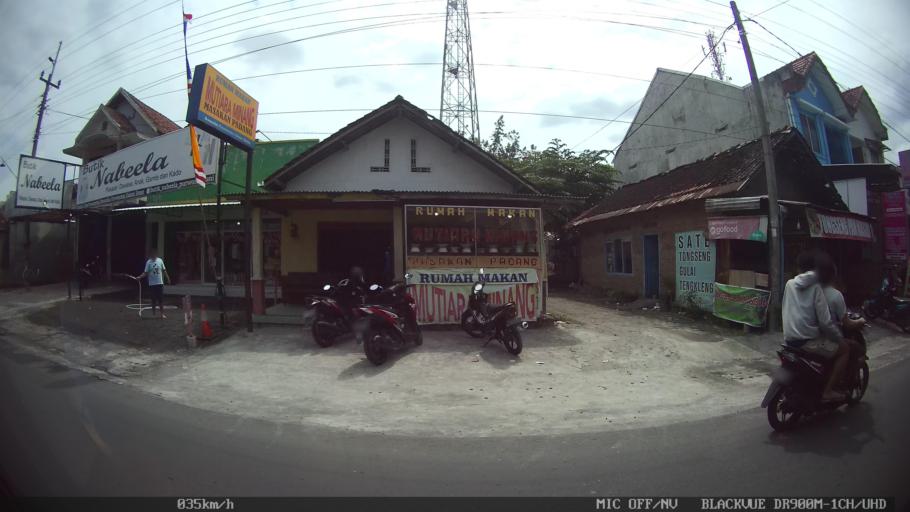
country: ID
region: Daerah Istimewa Yogyakarta
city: Depok
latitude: -7.7462
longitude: 110.4496
